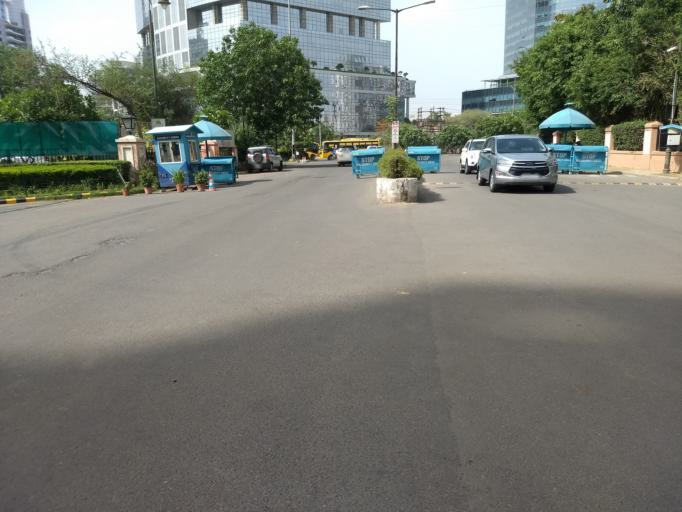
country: IN
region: Haryana
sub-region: Gurgaon
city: Gurgaon
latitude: 28.4493
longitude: 77.0962
